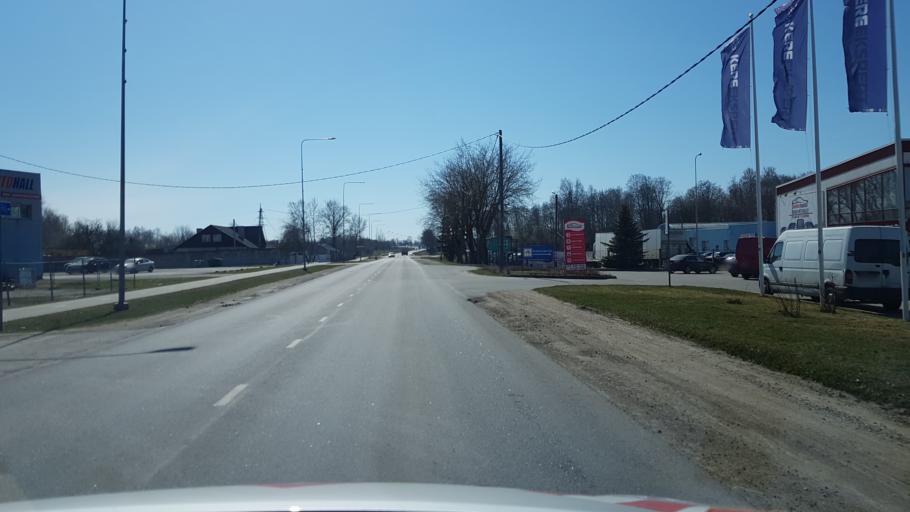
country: EE
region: Ida-Virumaa
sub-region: Johvi vald
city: Johvi
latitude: 59.3501
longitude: 27.4082
